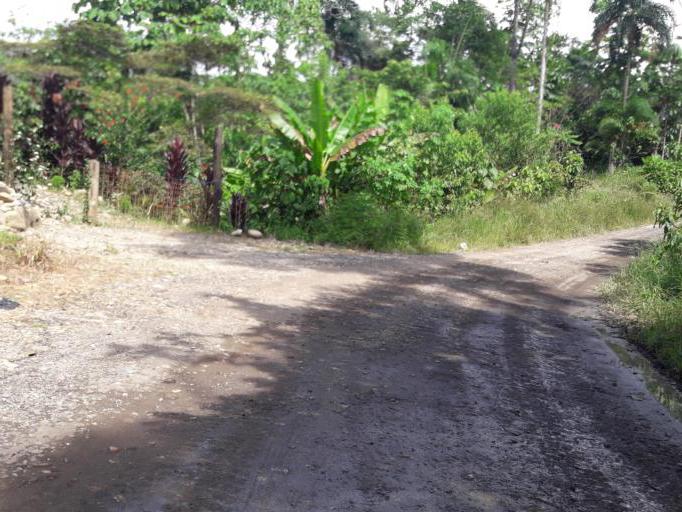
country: EC
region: Napo
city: Tena
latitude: -0.9563
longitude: -77.8222
